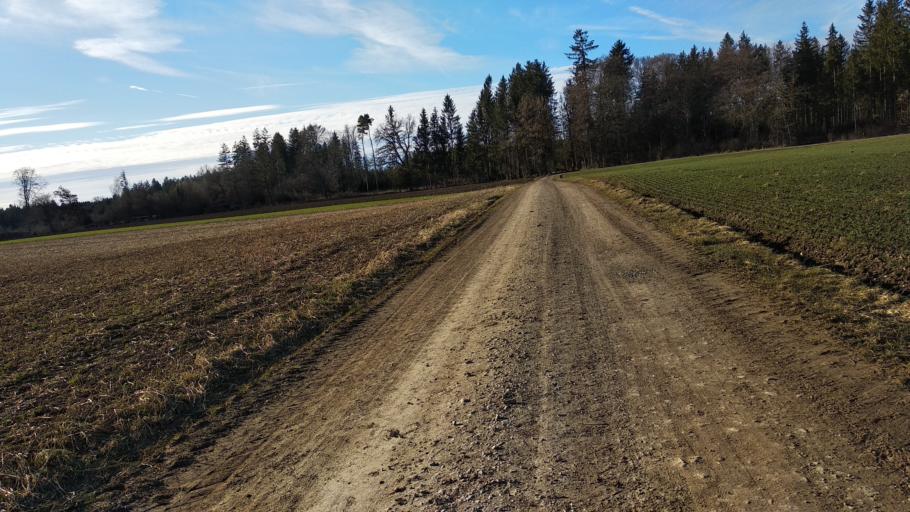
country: DE
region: Bavaria
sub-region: Upper Bavaria
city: Aying
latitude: 47.9826
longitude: 11.7678
